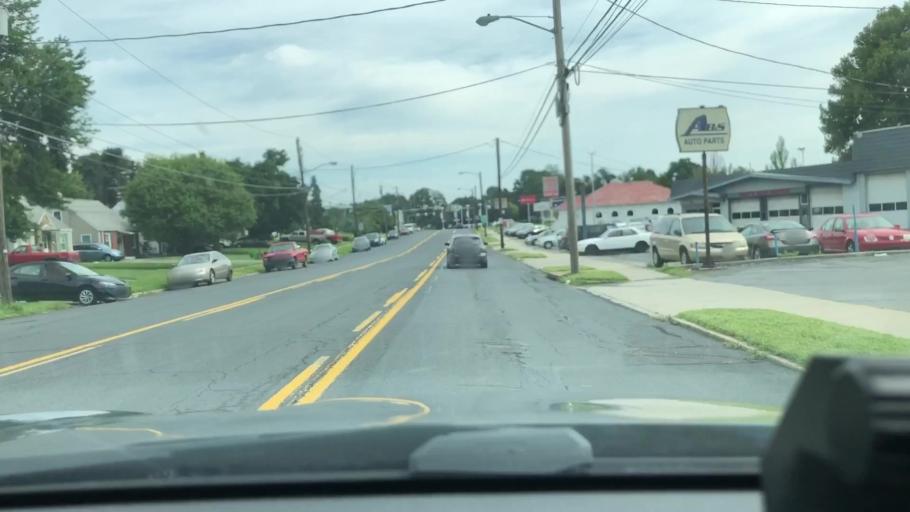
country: US
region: Pennsylvania
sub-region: Lehigh County
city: Allentown
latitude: 40.5807
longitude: -75.4791
